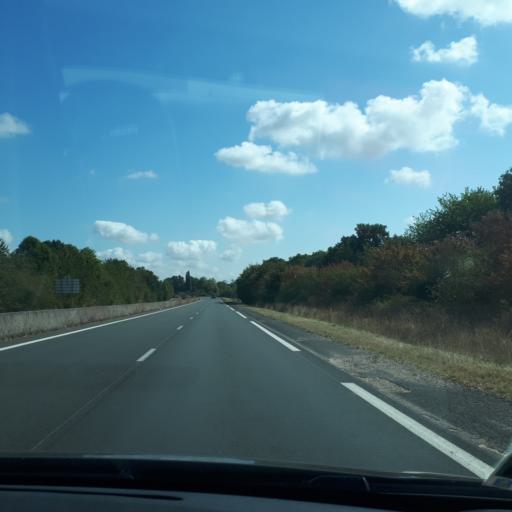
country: FR
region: Centre
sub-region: Departement du Loir-et-Cher
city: Moree
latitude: 47.8870
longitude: 1.1738
